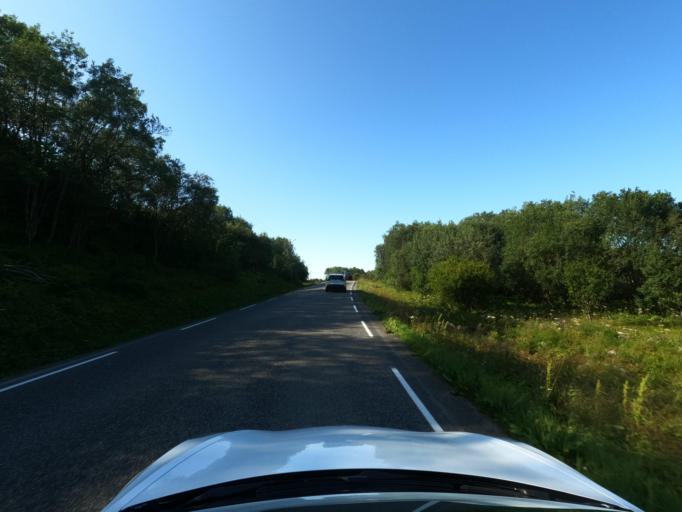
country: NO
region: Nordland
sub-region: Vestvagoy
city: Evjen
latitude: 68.2867
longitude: 13.8865
